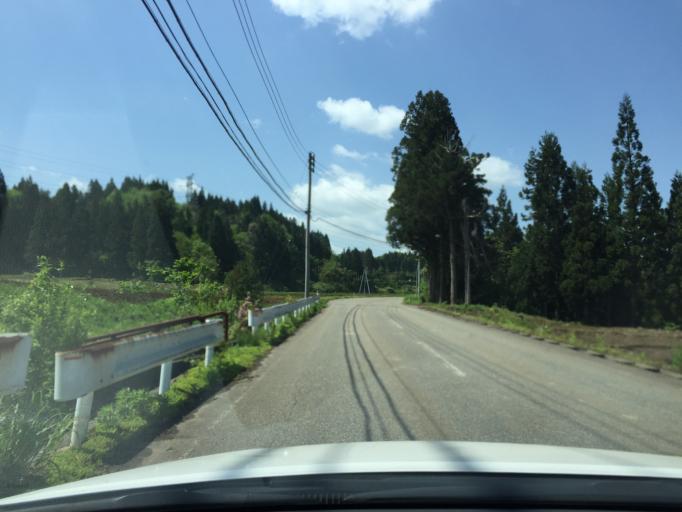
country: JP
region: Niigata
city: Tochio-honcho
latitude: 37.4870
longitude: 139.0525
